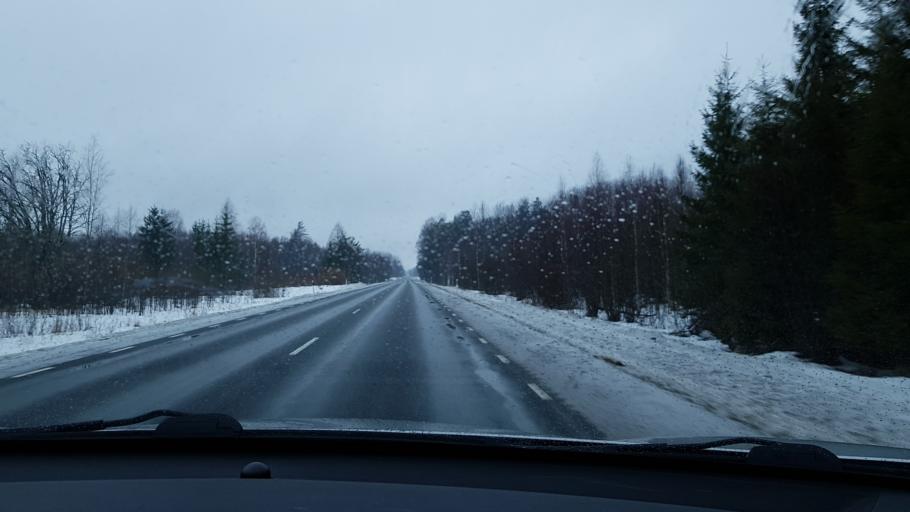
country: EE
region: Jaervamaa
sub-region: Tueri vald
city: Sarevere
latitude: 58.8025
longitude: 25.2269
